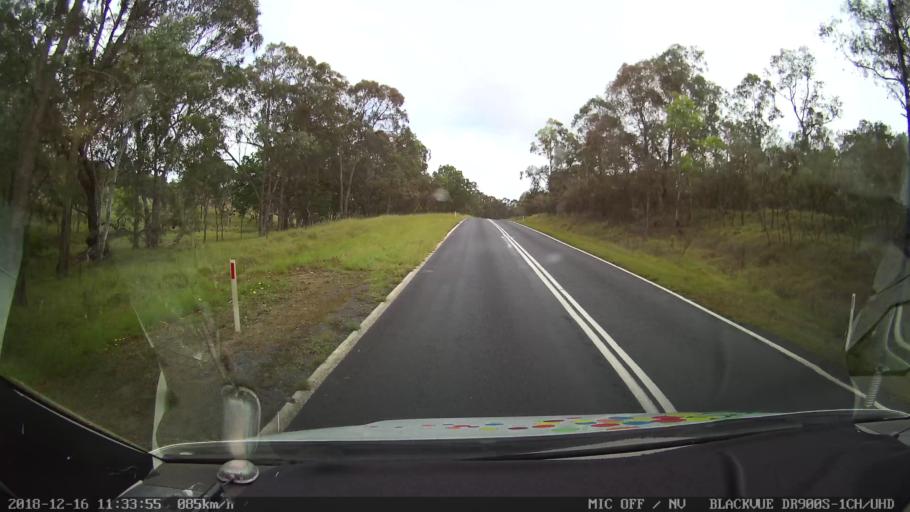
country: AU
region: New South Wales
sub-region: Tenterfield Municipality
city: Carrolls Creek
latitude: -29.0043
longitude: 152.1503
